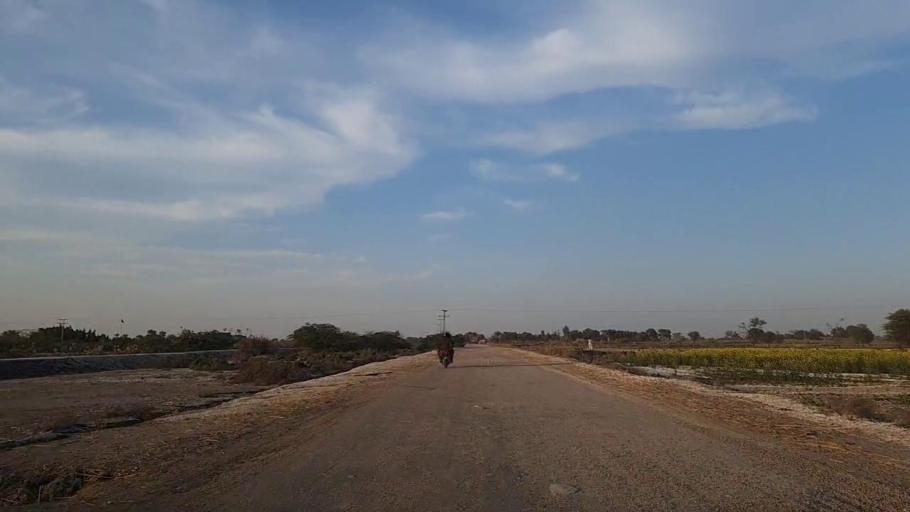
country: PK
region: Sindh
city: Bandhi
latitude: 26.5941
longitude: 68.3412
